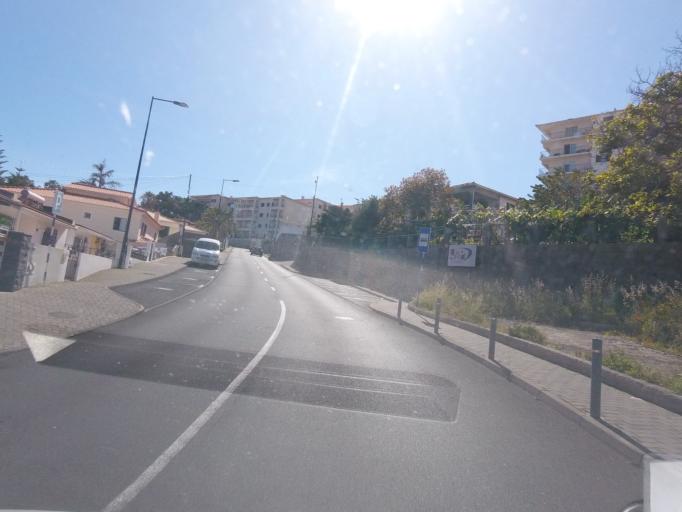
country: PT
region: Madeira
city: Canico
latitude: 32.6444
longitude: -16.8542
